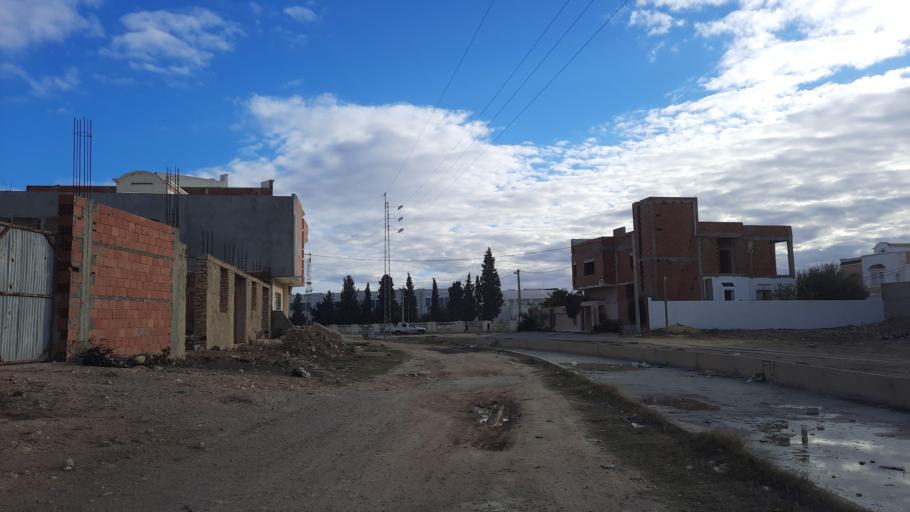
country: TN
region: Al Mahdiyah
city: El Jem
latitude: 35.2870
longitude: 10.7040
